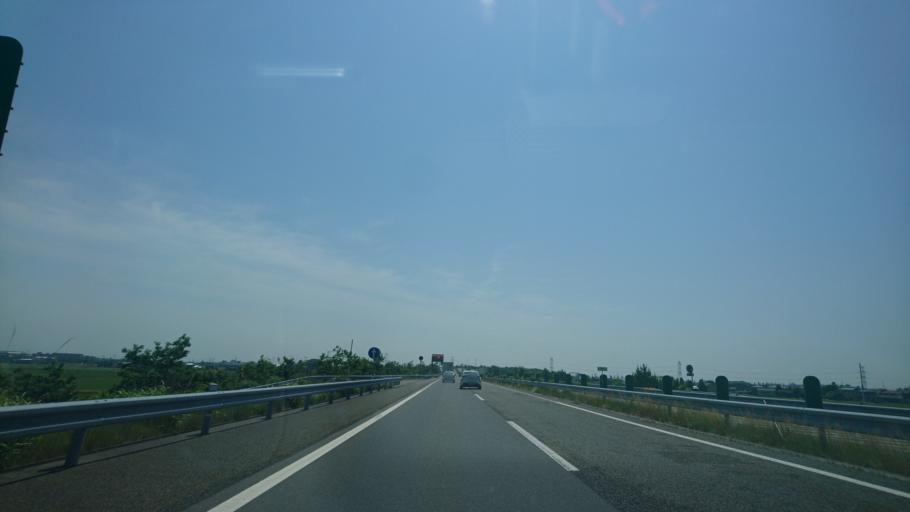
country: JP
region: Niigata
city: Shibata
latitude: 37.9676
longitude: 139.2969
